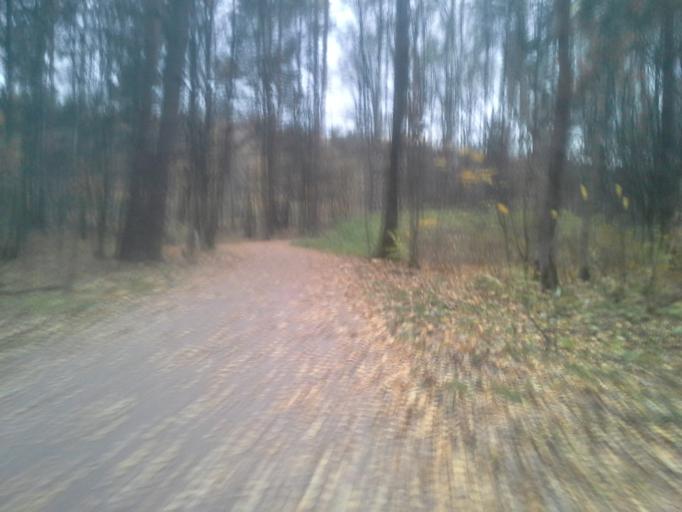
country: RU
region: Moskovskaya
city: Zarech'ye
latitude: 55.6674
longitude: 37.3871
